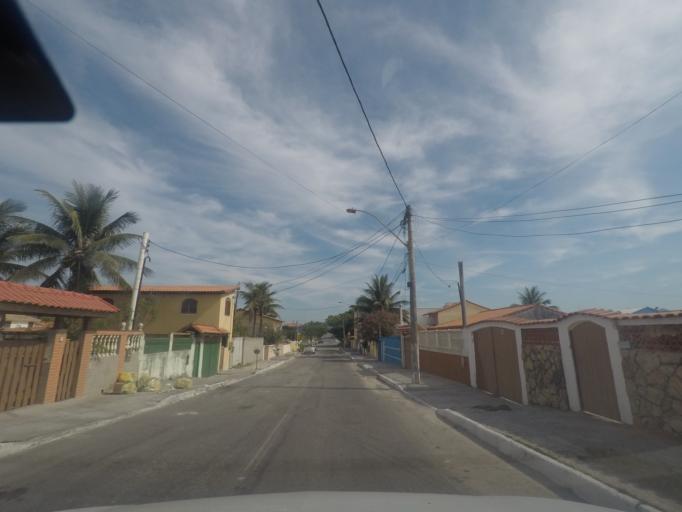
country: BR
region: Rio de Janeiro
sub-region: Marica
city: Marica
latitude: -22.9607
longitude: -42.8156
